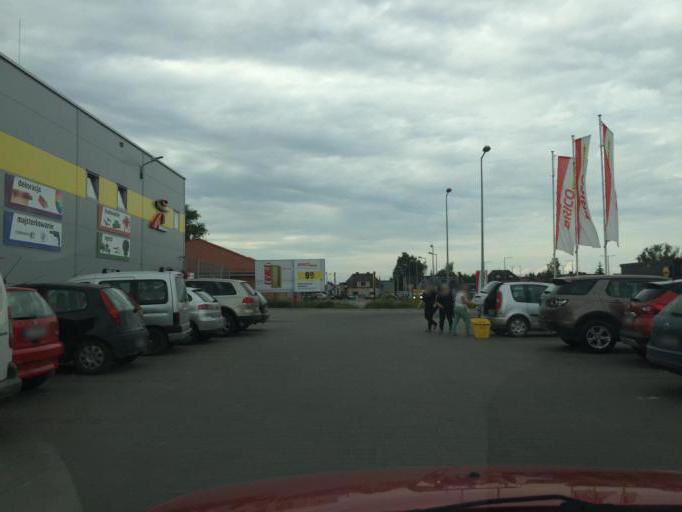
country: PL
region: Greater Poland Voivodeship
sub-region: Powiat poznanski
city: Plewiska
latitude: 52.3948
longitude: 16.8016
